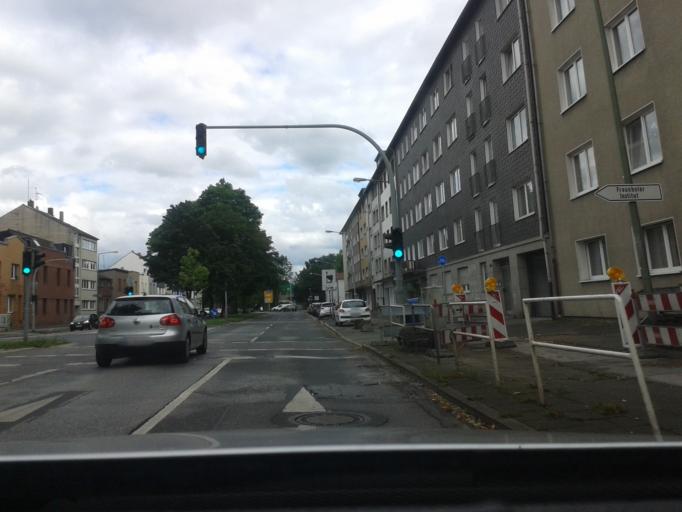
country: DE
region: North Rhine-Westphalia
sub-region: Regierungsbezirk Dusseldorf
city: Duisburg
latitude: 51.4172
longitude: 6.7900
